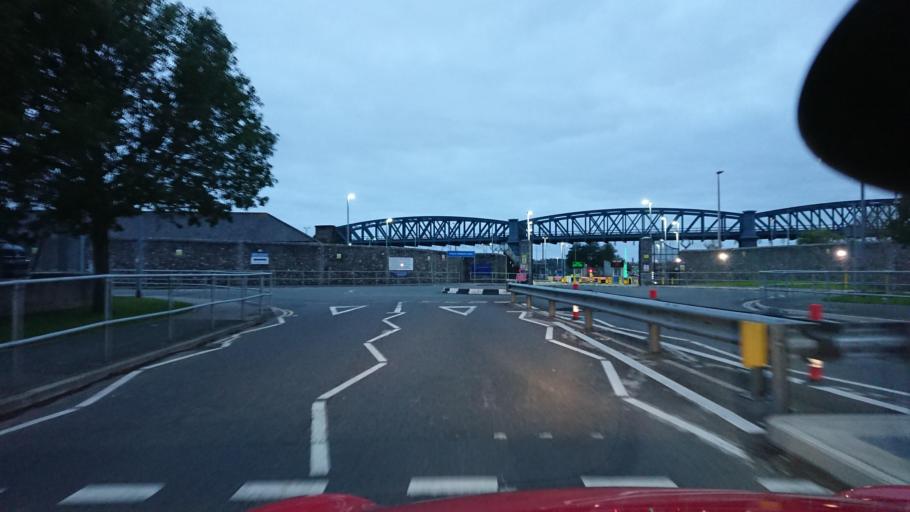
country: GB
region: England
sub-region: Cornwall
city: Torpoint
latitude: 50.3952
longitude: -4.1800
